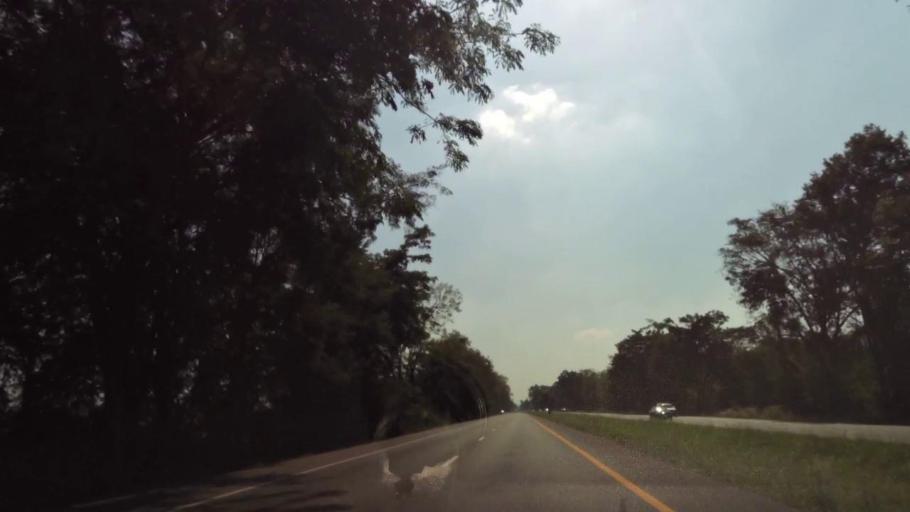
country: TH
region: Phichit
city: Bueng Na Rang
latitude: 16.2132
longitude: 100.1271
